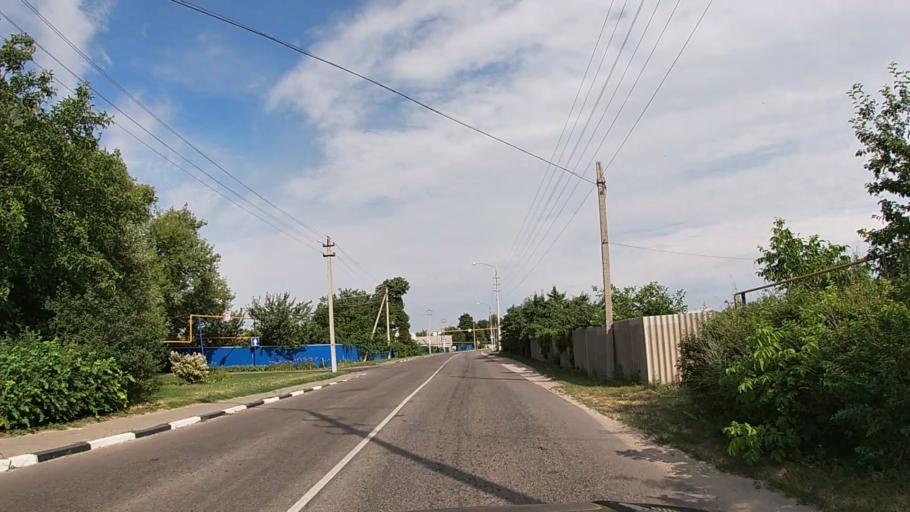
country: RU
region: Belgorod
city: Krasnaya Yaruga
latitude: 50.8000
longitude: 35.6621
